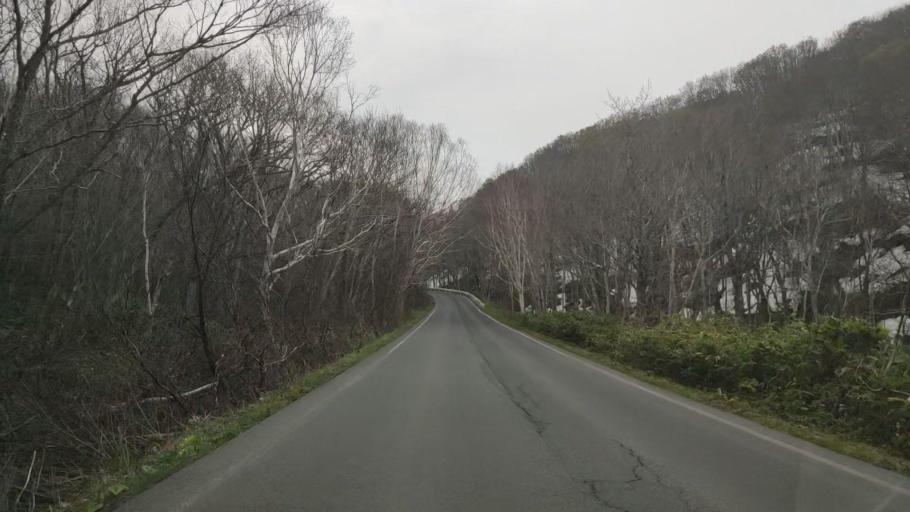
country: JP
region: Aomori
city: Aomori Shi
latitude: 40.6919
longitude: 140.9111
